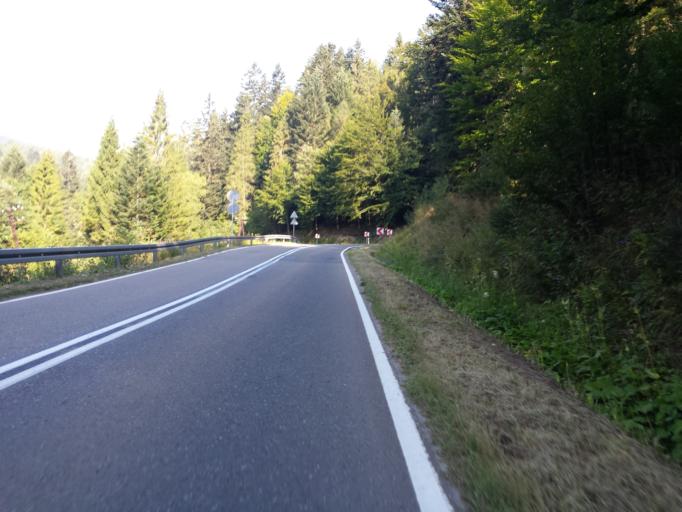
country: PL
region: Subcarpathian Voivodeship
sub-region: Powiat leski
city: Cisna
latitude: 49.2240
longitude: 22.3104
